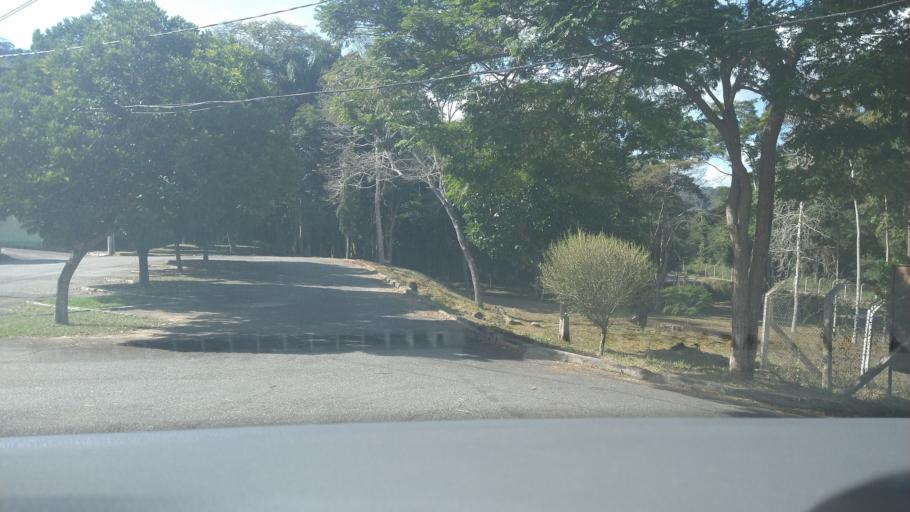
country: BR
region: Minas Gerais
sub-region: Vicosa
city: Vicosa
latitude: -20.7702
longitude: -42.8754
